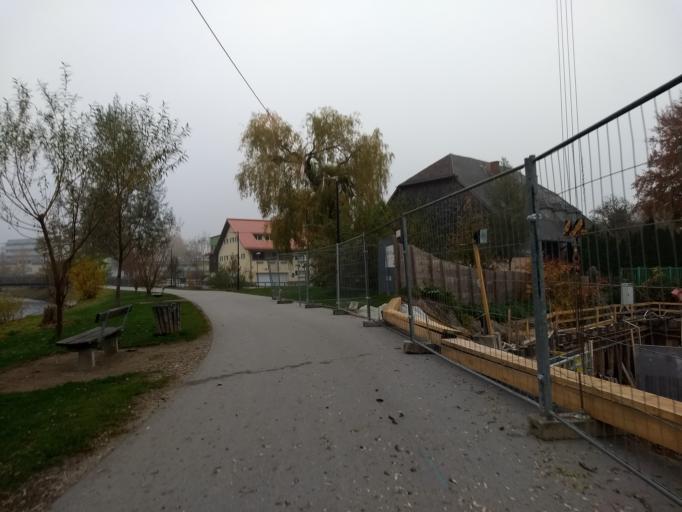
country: AT
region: Salzburg
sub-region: Salzburg Stadt
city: Salzburg
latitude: 47.8098
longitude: 13.0222
